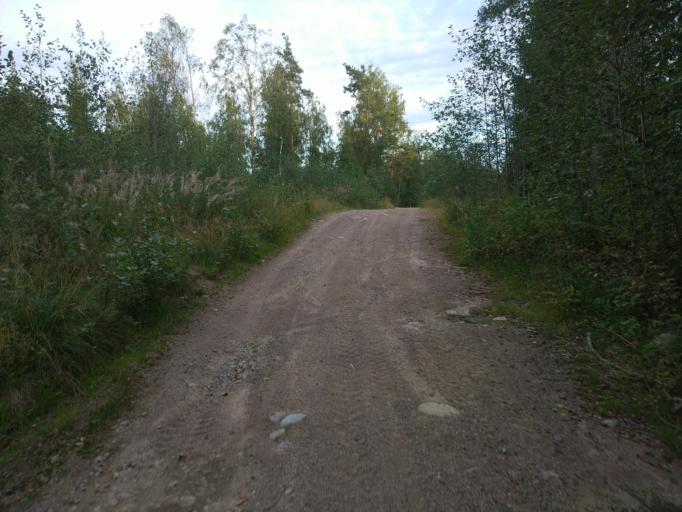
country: RU
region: Leningrad
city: Kuznechnoye
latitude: 61.1157
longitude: 29.6054
